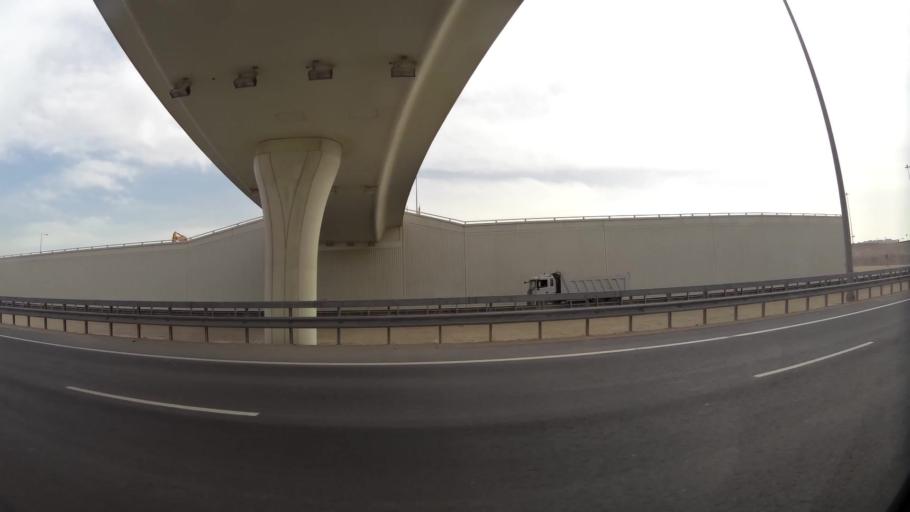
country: QA
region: Baladiyat ar Rayyan
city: Ar Rayyan
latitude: 25.3199
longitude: 51.3545
